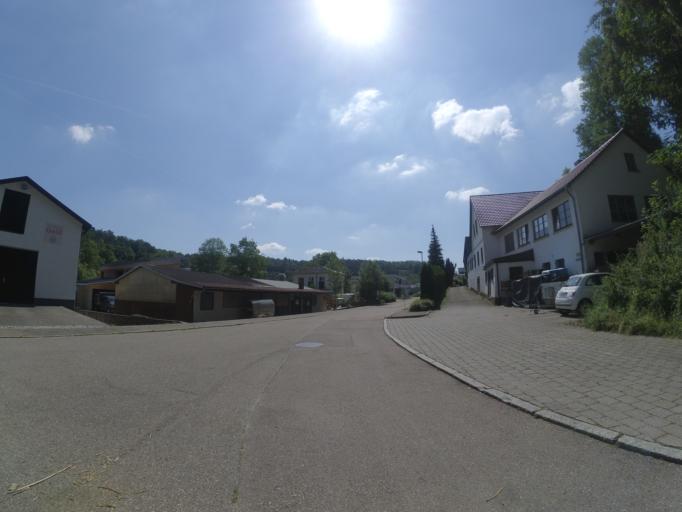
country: DE
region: Baden-Wuerttemberg
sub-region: Tuebingen Region
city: Dornstadt
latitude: 48.4271
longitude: 9.8933
